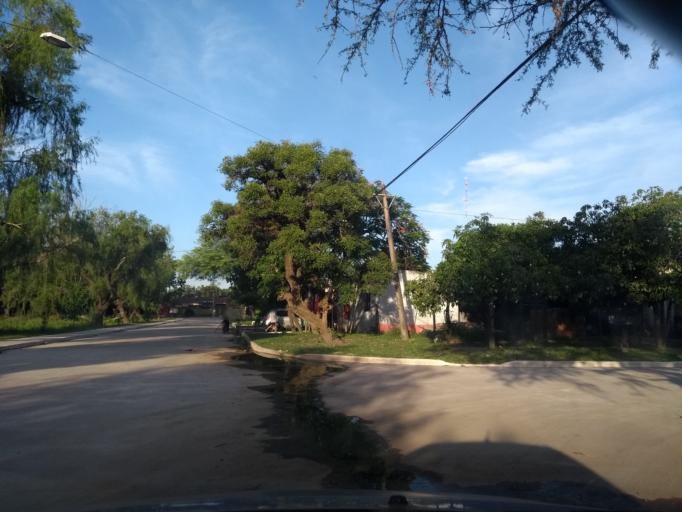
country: AR
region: Chaco
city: Resistencia
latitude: -27.4742
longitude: -58.9642
